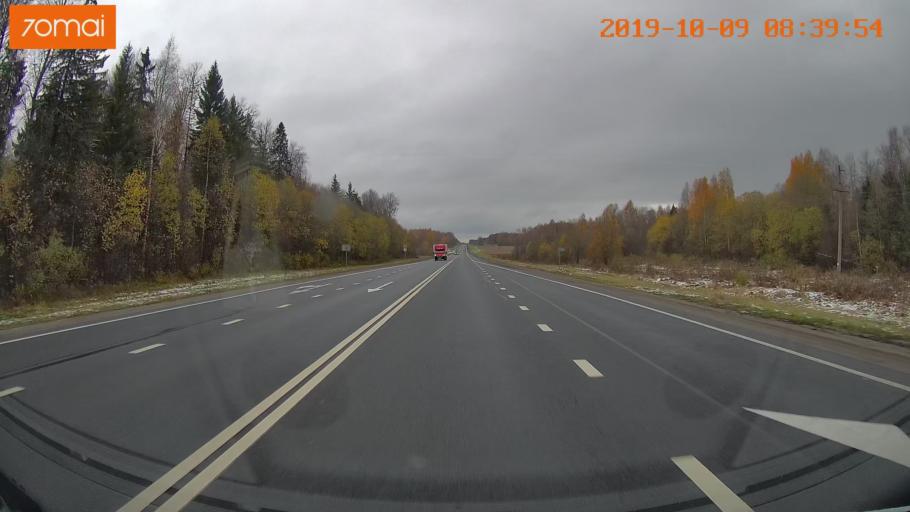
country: RU
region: Vologda
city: Gryazovets
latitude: 58.9784
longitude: 40.1473
